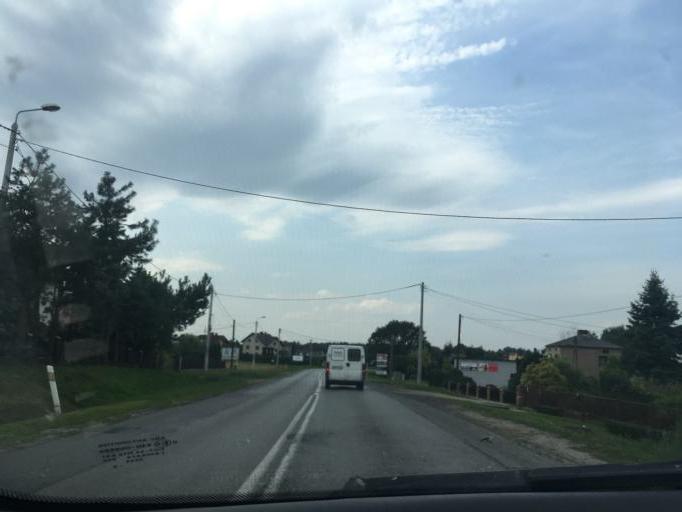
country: PL
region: Silesian Voivodeship
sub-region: Powiat raciborski
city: Pogrzebien
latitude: 50.0748
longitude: 18.3068
